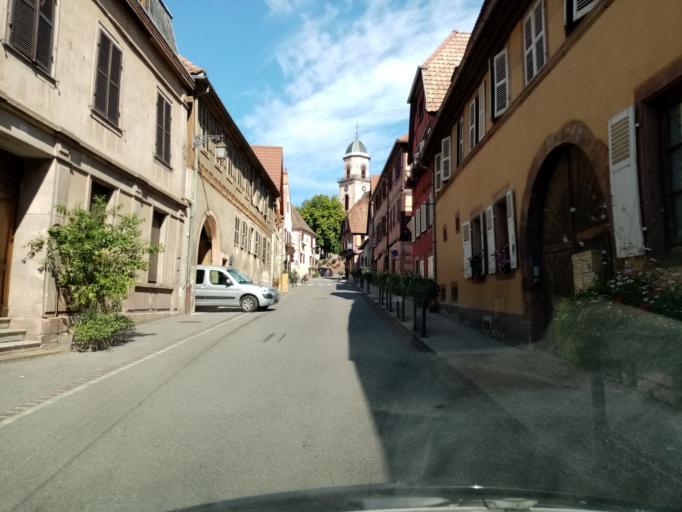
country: FR
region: Alsace
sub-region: Departement du Haut-Rhin
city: Saint-Hippolyte
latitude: 48.2329
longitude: 7.3691
